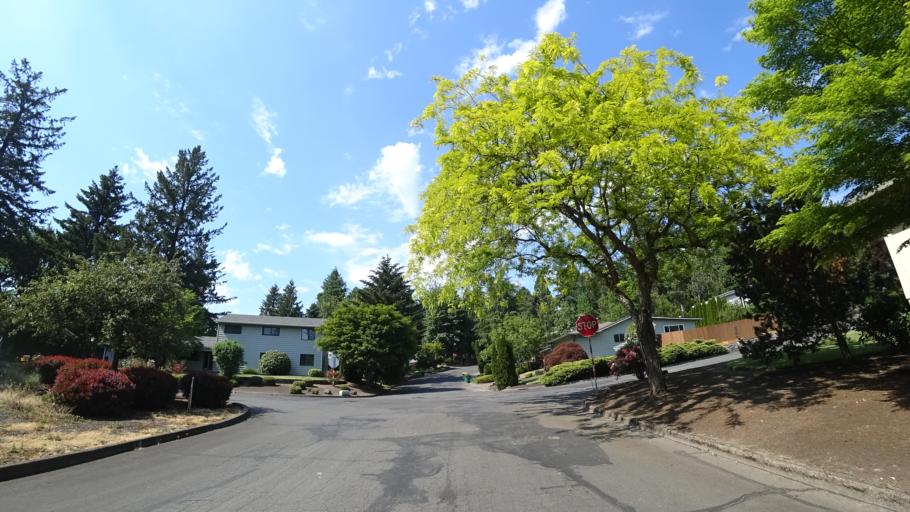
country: US
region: Oregon
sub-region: Washington County
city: Metzger
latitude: 45.4517
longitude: -122.7512
